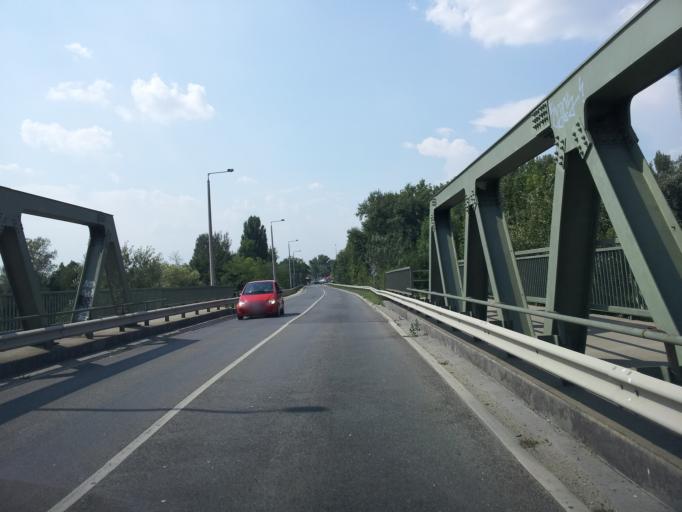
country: HU
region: Pest
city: Szigetszentmiklos
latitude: 47.3122
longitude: 19.0348
